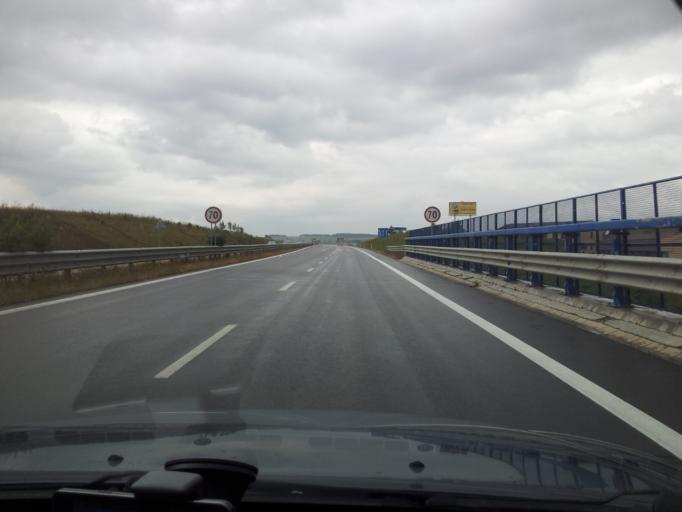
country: SK
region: Presovsky
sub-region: Okres Poprad
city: Poprad
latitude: 49.0958
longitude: 20.3402
